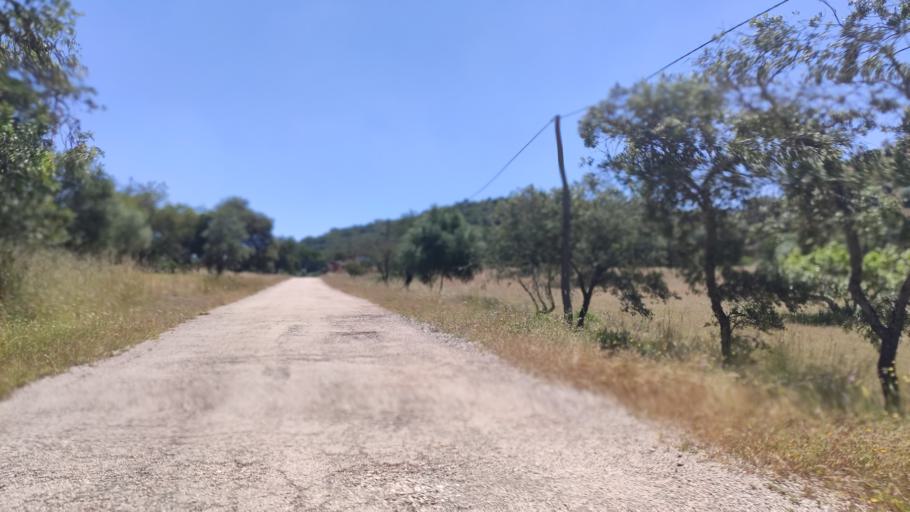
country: PT
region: Faro
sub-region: Sao Bras de Alportel
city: Sao Bras de Alportel
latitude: 37.1740
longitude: -7.9253
